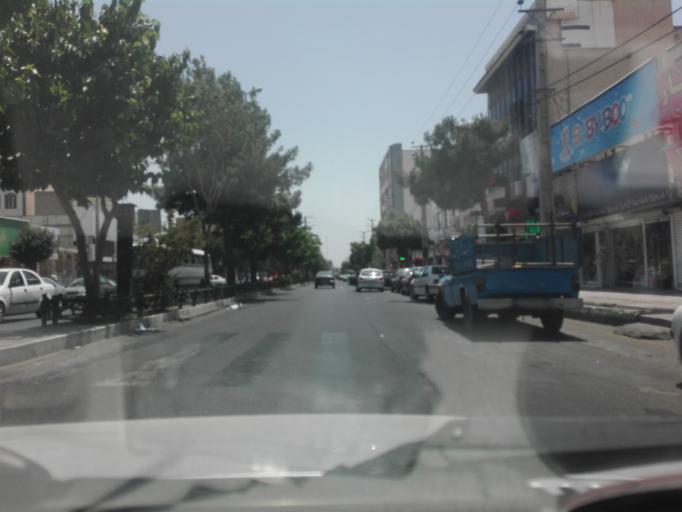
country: IR
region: Tehran
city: Shahre Jadide Andisheh
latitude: 35.7142
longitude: 50.9855
